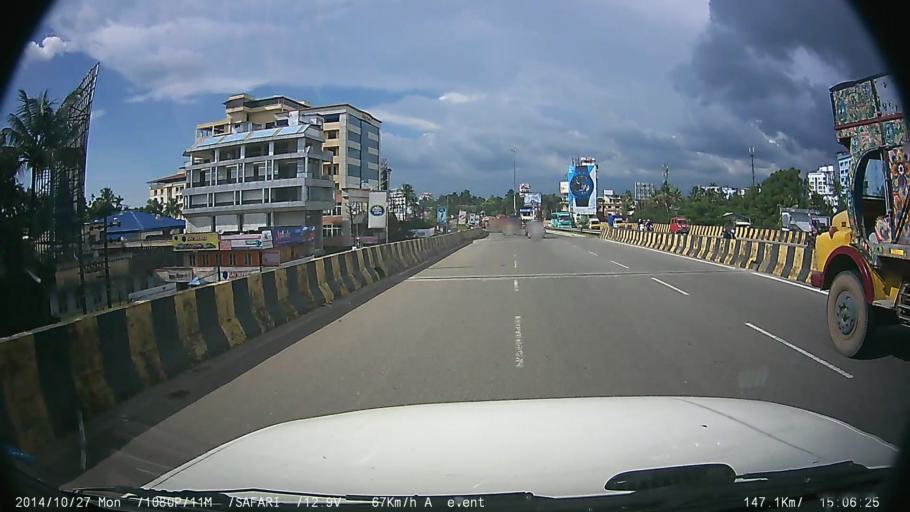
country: IN
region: Kerala
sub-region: Ernakulam
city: Aluva
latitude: 10.1082
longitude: 76.3497
